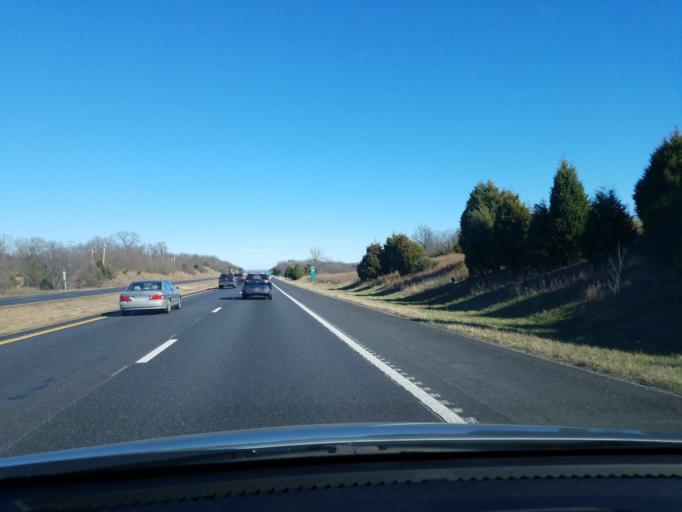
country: US
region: Missouri
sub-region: Taney County
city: Hollister
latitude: 36.5785
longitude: -93.2411
